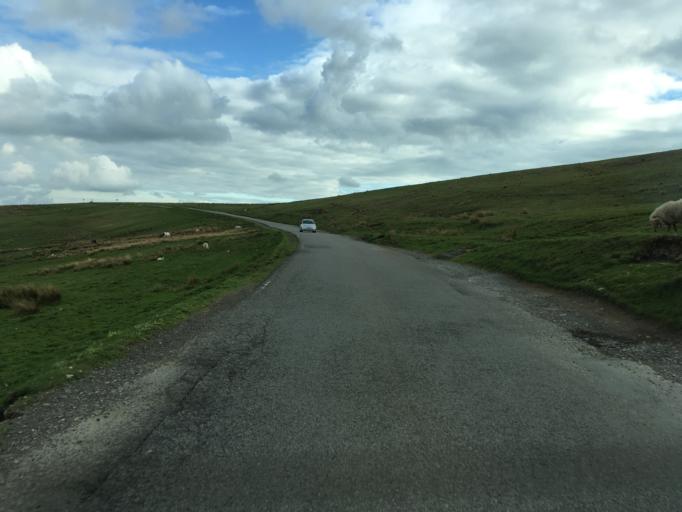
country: GB
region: Wales
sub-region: Caerphilly County Borough
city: Rhymney
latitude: 51.7245
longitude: -3.2977
